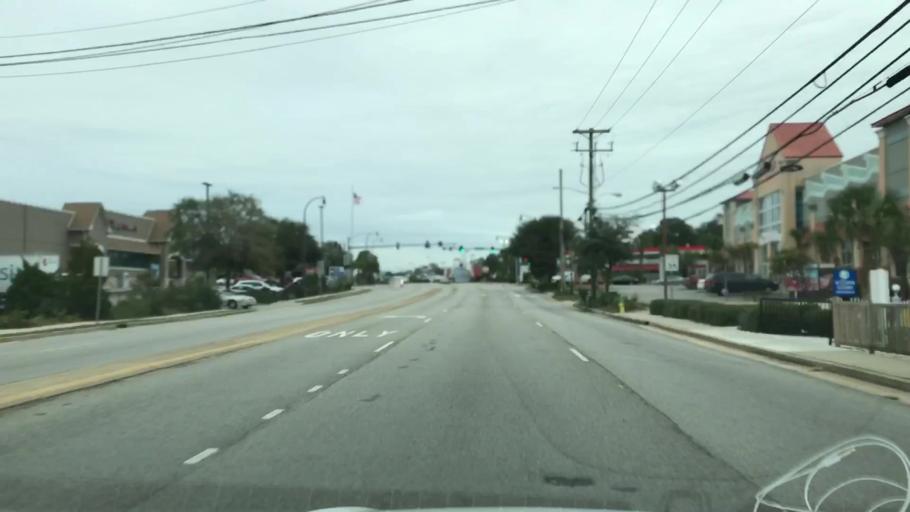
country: US
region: South Carolina
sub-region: Horry County
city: Myrtle Beach
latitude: 33.6837
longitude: -78.8929
